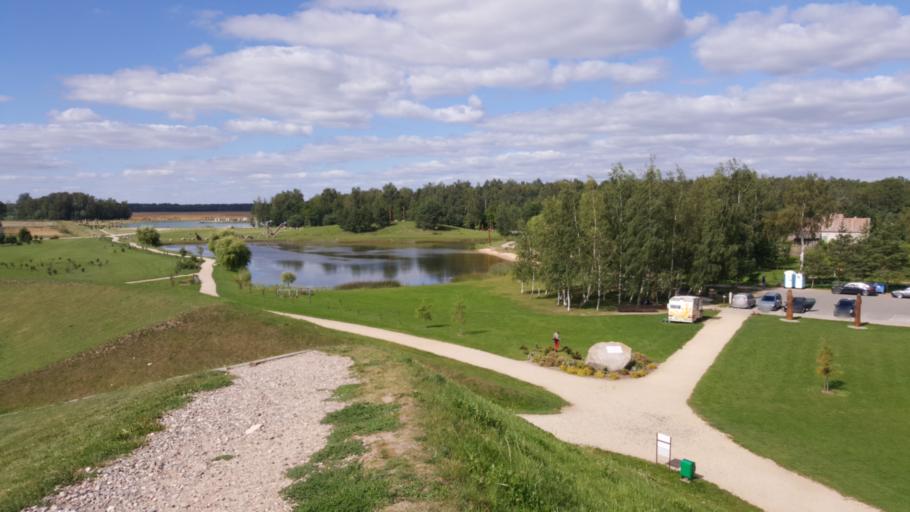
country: LT
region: Siauliu apskritis
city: Radviliskis
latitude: 56.0211
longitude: 23.5084
